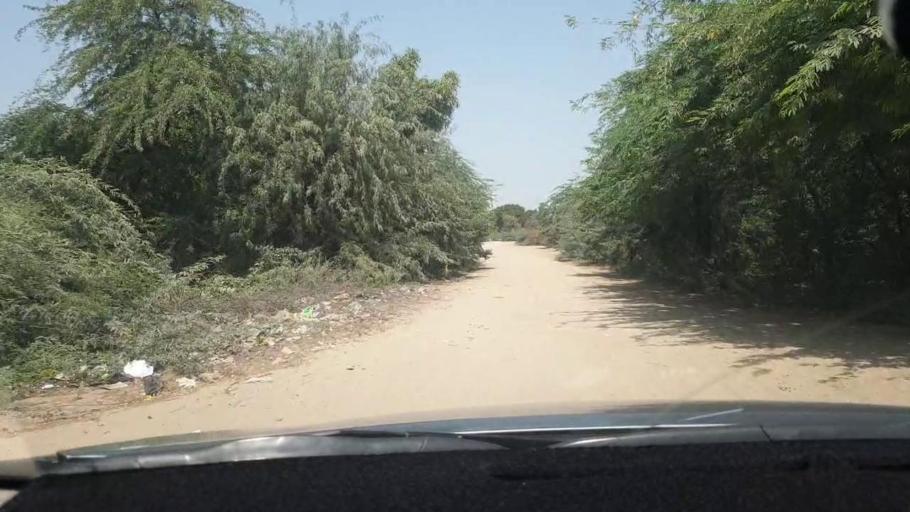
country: PK
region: Sindh
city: Tando Mittha Khan
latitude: 25.8525
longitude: 69.4245
